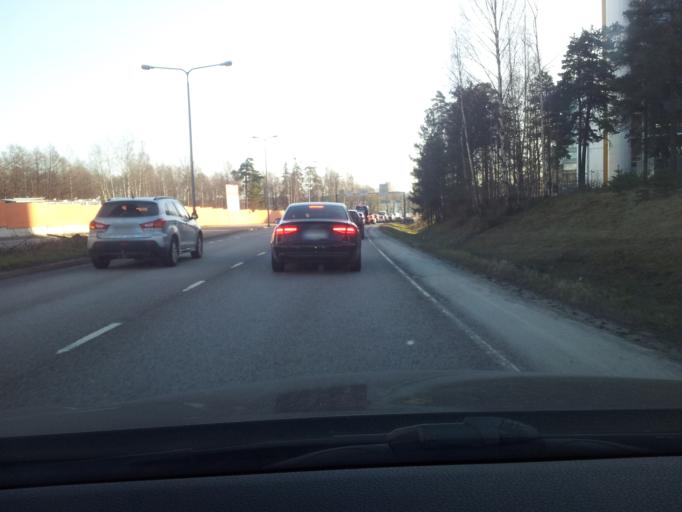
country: FI
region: Uusimaa
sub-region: Helsinki
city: Otaniemi
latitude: 60.1787
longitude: 24.8322
